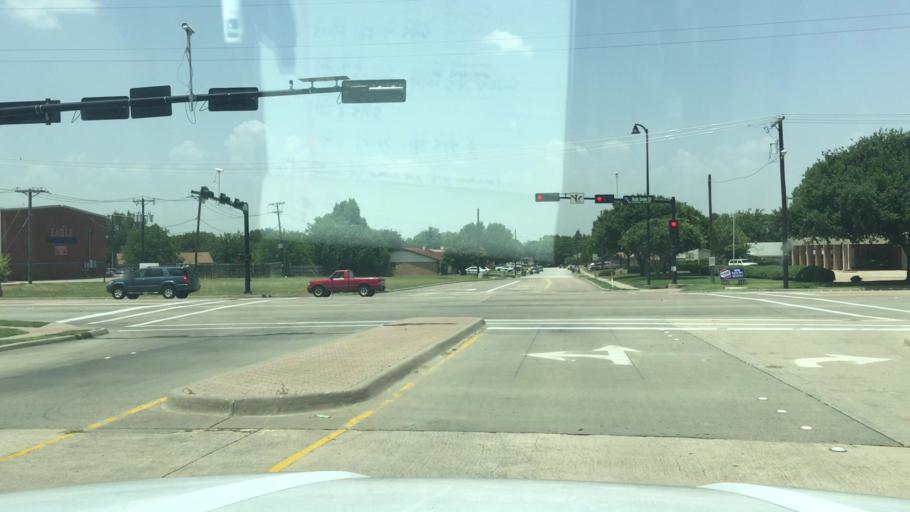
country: US
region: Texas
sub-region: Tarrant County
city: Watauga
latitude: 32.8555
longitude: -97.2379
